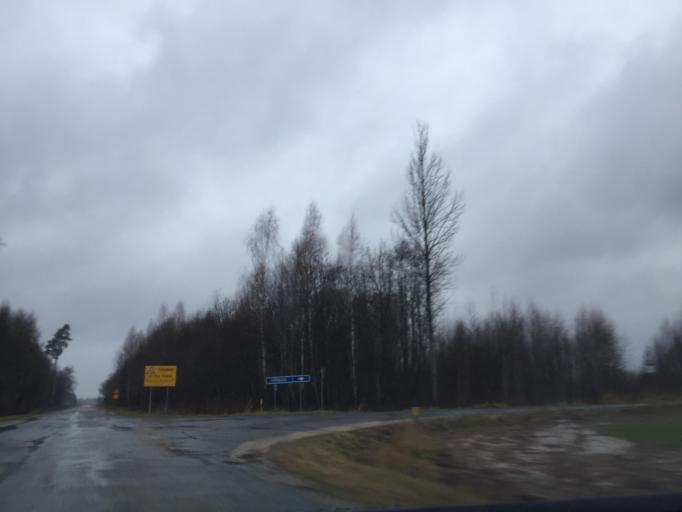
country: LV
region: Salacgrivas
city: Salacgriva
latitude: 57.7619
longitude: 24.5561
